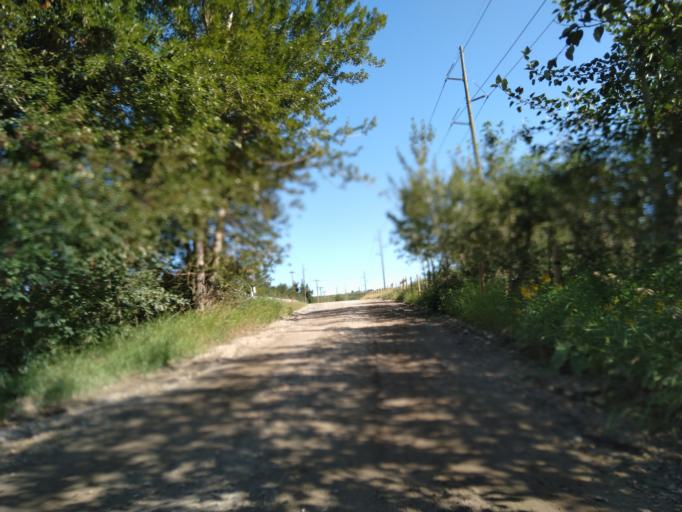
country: CA
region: Alberta
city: Calgary
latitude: 51.1001
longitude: -114.2343
